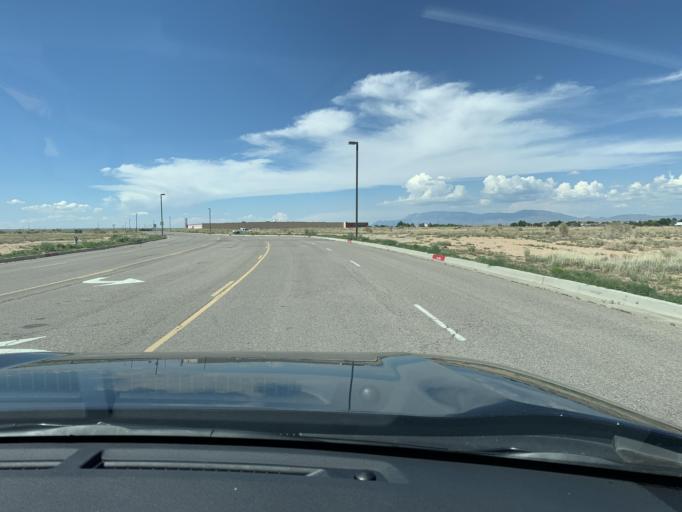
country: US
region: New Mexico
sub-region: Valencia County
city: Los Lunas
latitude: 34.8202
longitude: -106.7625
